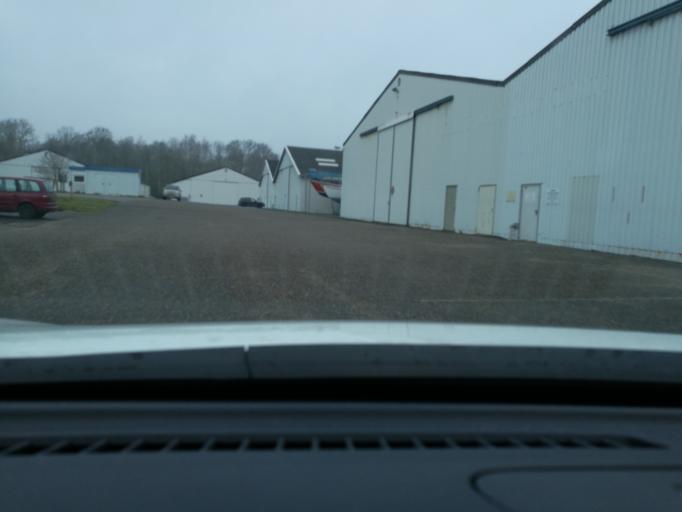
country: DE
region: Schleswig-Holstein
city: Borgstedt
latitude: 54.3293
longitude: 9.7215
